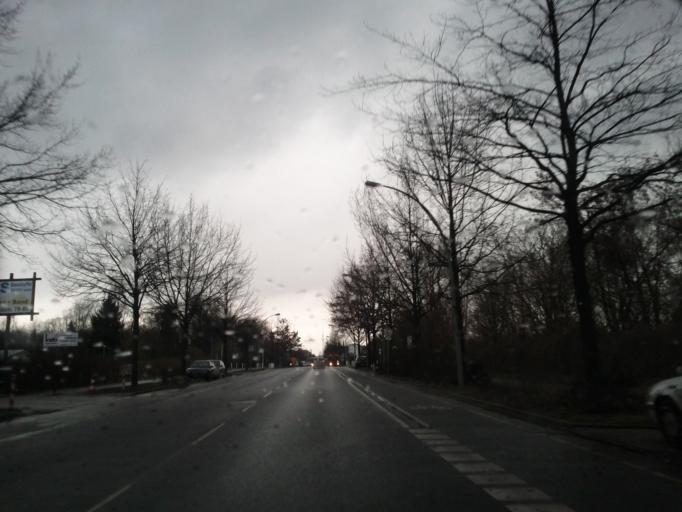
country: DE
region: Berlin
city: Plaenterwald
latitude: 52.4811
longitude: 13.4651
